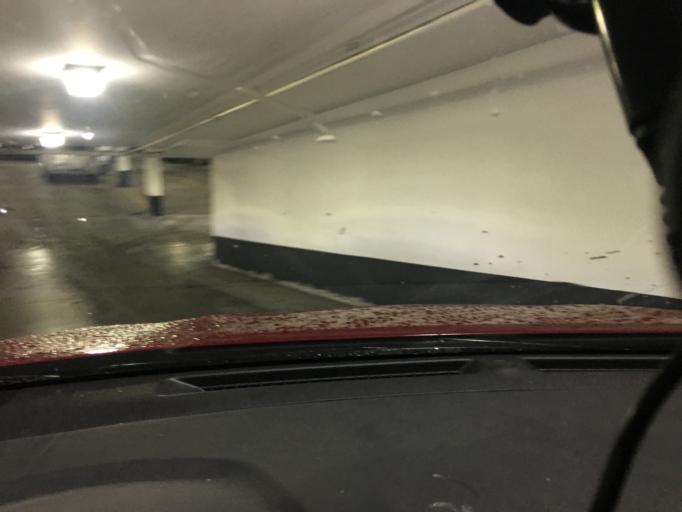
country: CA
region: Ontario
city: Scarborough
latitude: 43.7740
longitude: -79.2577
